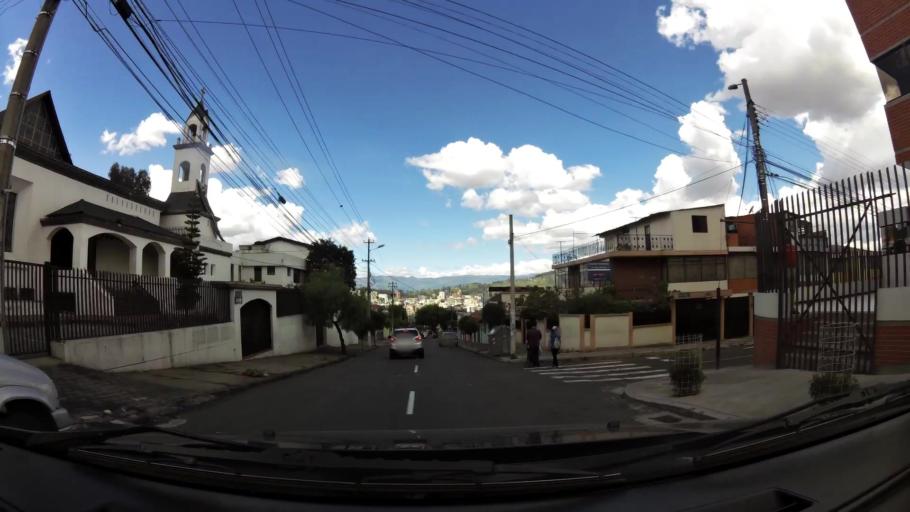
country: EC
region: Pichincha
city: Quito
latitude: -0.1899
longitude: -78.5009
